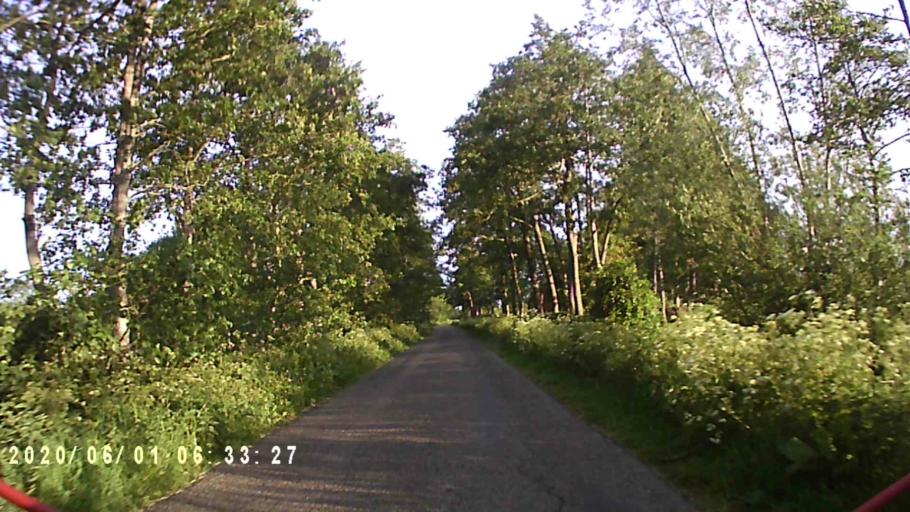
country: NL
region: Friesland
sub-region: Gemeente Kollumerland en Nieuwkruisland
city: Kollum
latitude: 53.2767
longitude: 6.1698
